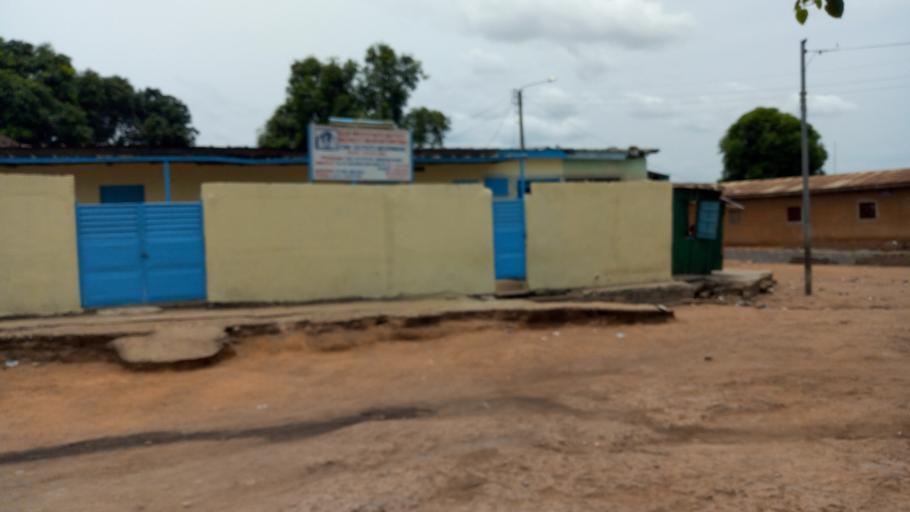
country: CI
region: Vallee du Bandama
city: Bouake
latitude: 7.6912
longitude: -5.0358
